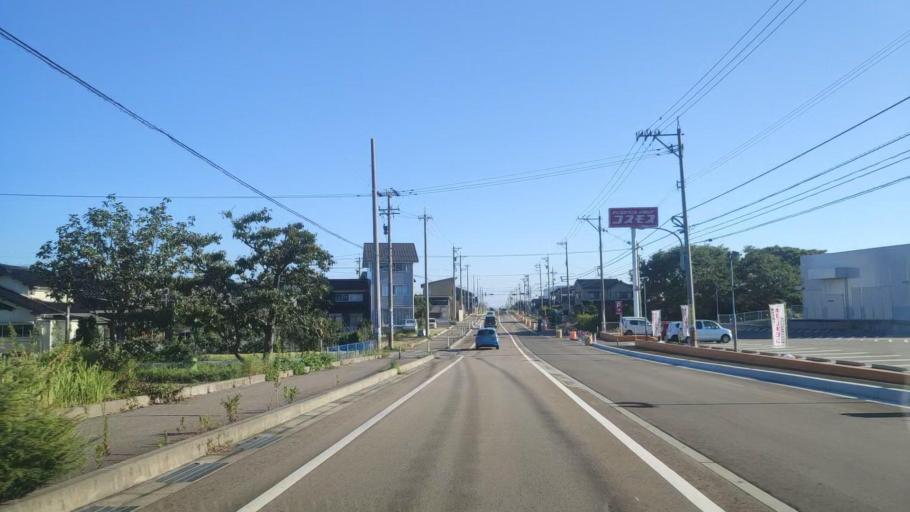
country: JP
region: Ishikawa
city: Tsubata
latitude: 36.7366
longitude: 136.7030
